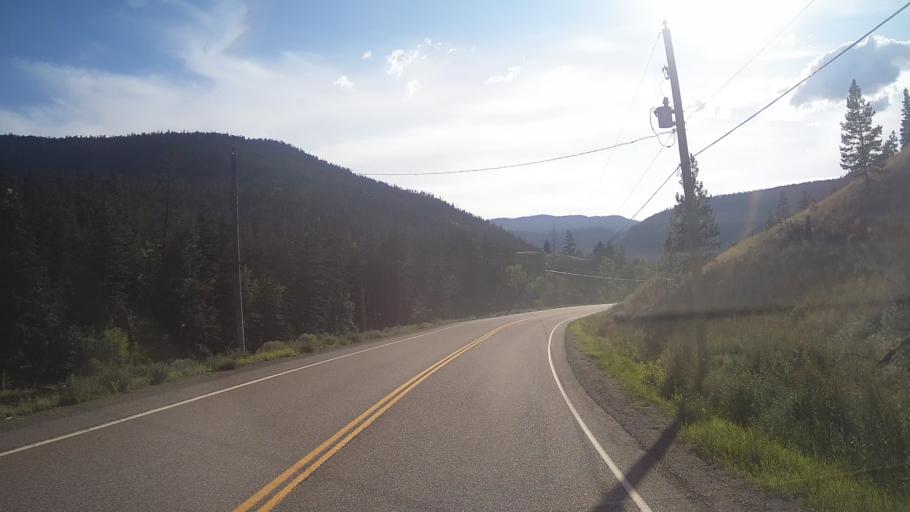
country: CA
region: British Columbia
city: Cache Creek
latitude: 50.8842
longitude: -121.4734
